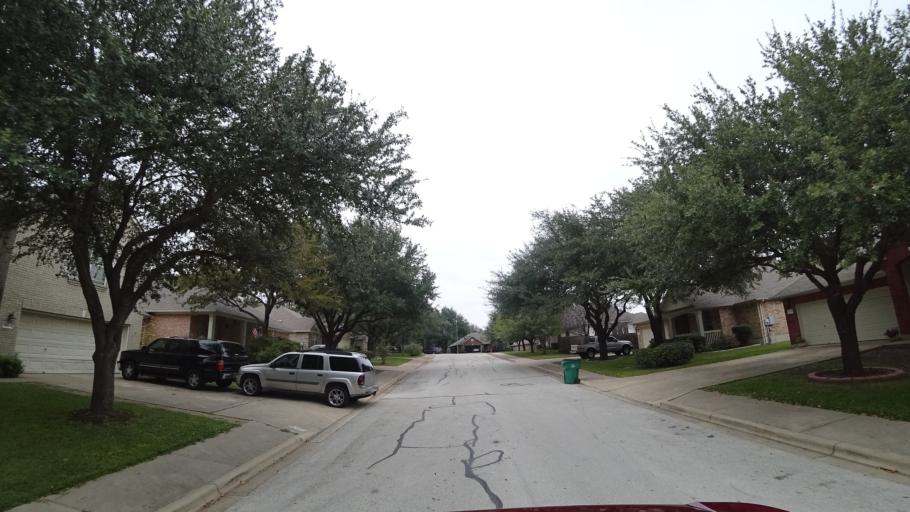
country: US
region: Texas
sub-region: Travis County
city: Wells Branch
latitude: 30.4502
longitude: -97.6829
